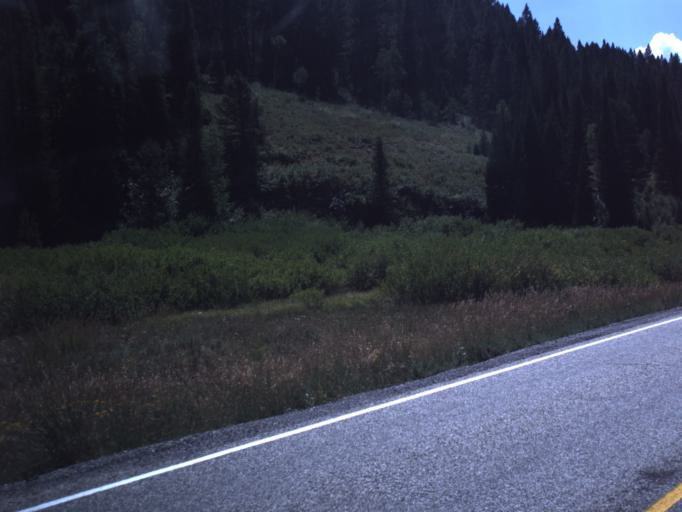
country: US
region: Utah
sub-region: Cache County
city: Richmond
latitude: 41.9595
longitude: -111.5372
